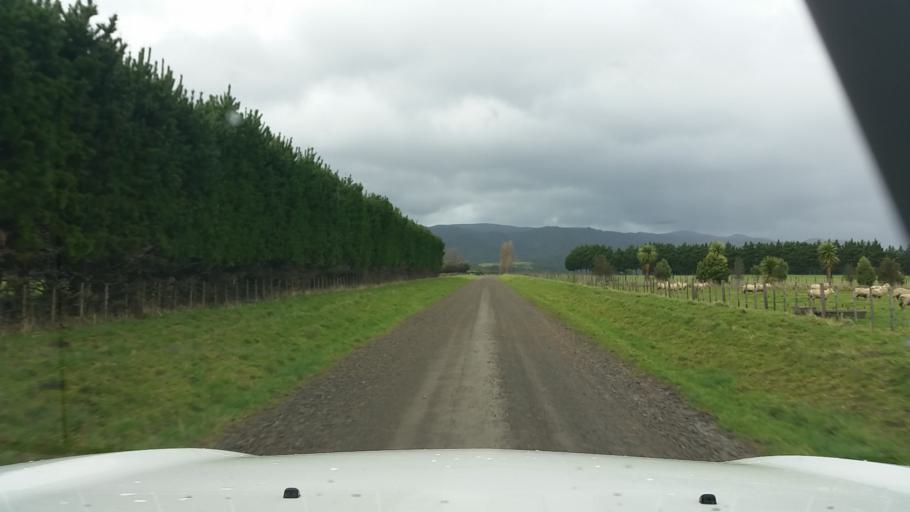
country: NZ
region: Wellington
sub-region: Upper Hutt City
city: Upper Hutt
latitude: -41.3471
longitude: 175.2358
